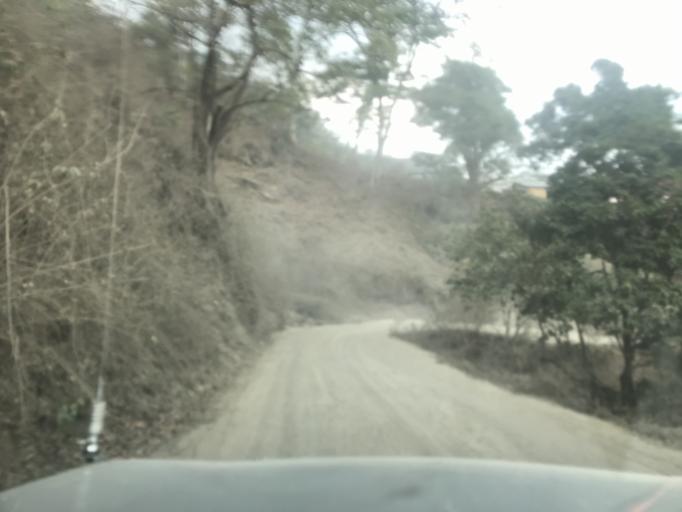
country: TL
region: Ermera
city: Gleno
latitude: -8.7633
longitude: 125.4363
